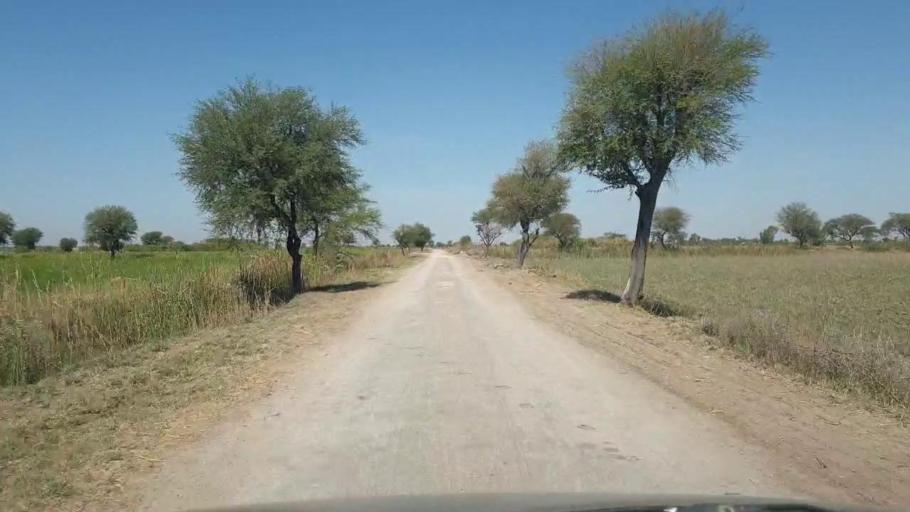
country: PK
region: Sindh
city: Dhoro Naro
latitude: 25.4396
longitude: 69.6174
